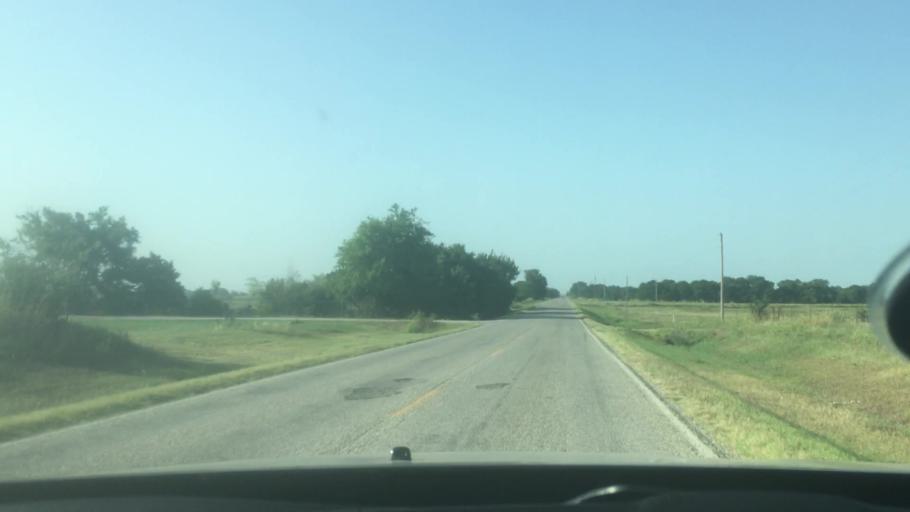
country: US
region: Oklahoma
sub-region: Johnston County
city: Tishomingo
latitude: 34.3105
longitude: -96.4248
